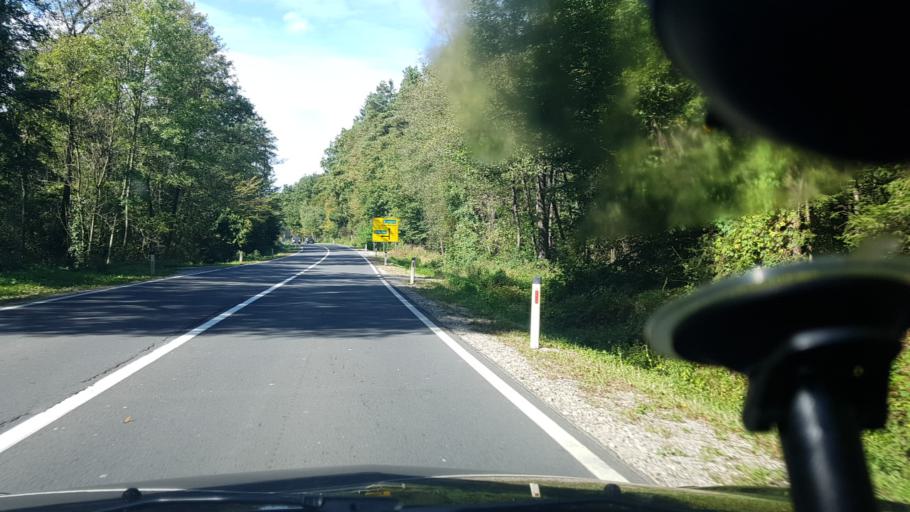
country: SI
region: Slovenska Bistrica
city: Zgornja Polskava
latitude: 46.3977
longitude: 15.6098
